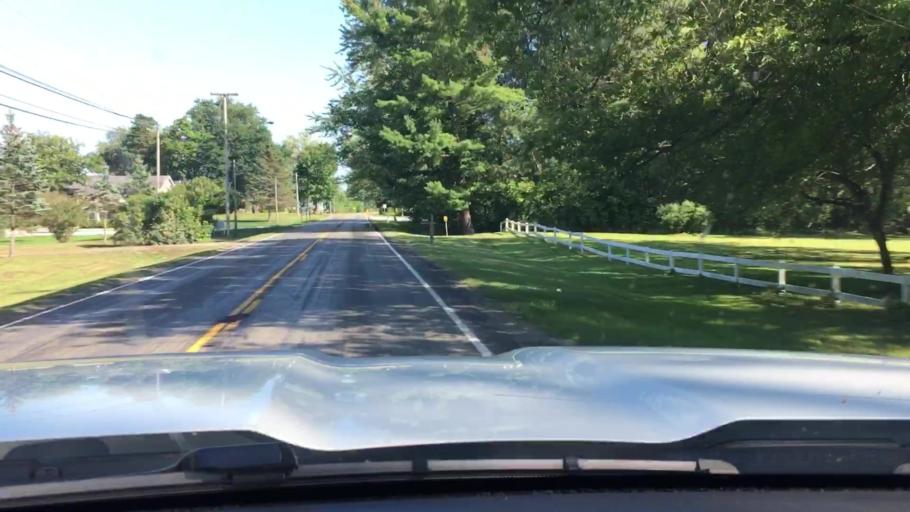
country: US
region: Michigan
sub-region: Muskegon County
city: Ravenna
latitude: 43.1852
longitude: -85.9335
